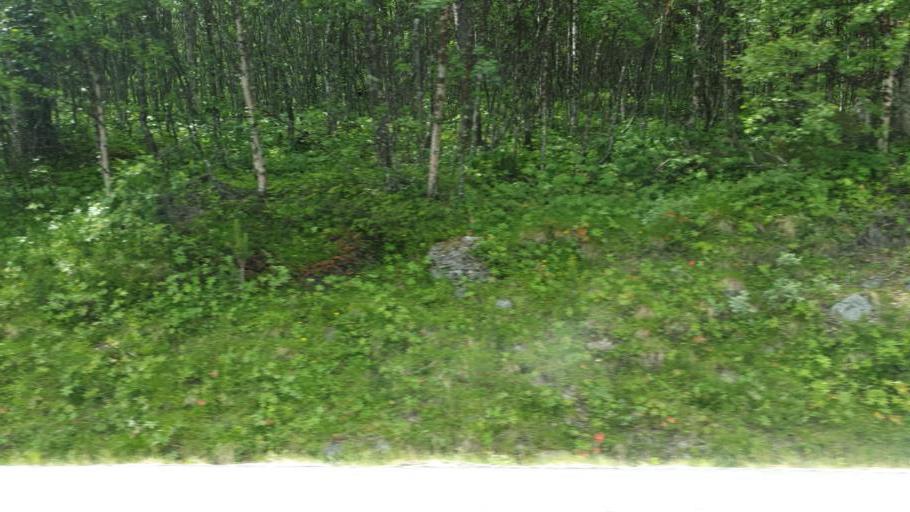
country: NO
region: Oppland
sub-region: Vaga
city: Vagamo
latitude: 61.7510
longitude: 9.0782
